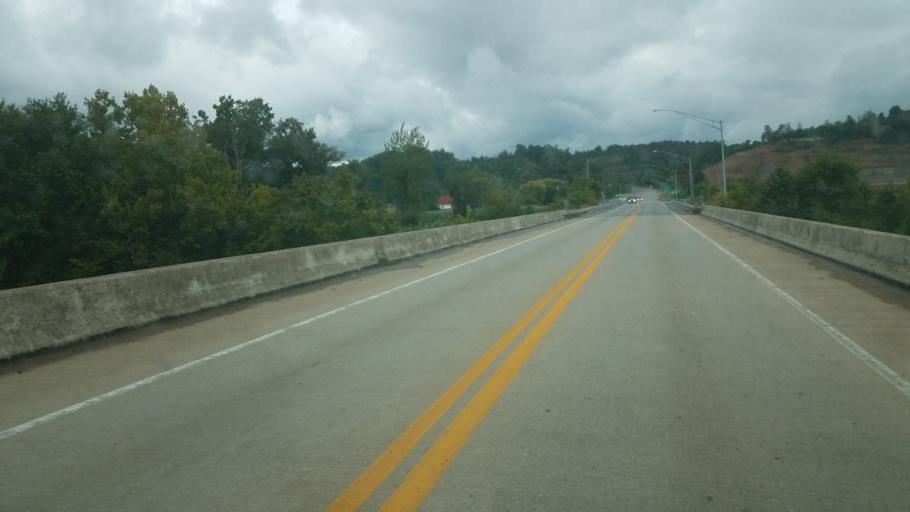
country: US
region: Ohio
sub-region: Scioto County
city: Franklin Furnace
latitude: 38.6465
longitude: -82.8700
